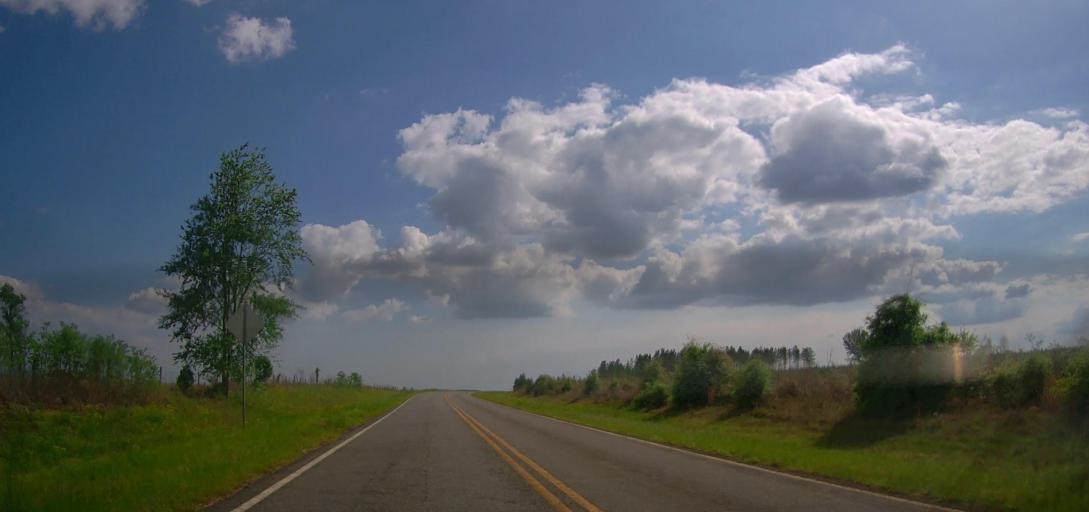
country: US
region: Georgia
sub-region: Laurens County
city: East Dublin
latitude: 32.7298
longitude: -82.9097
